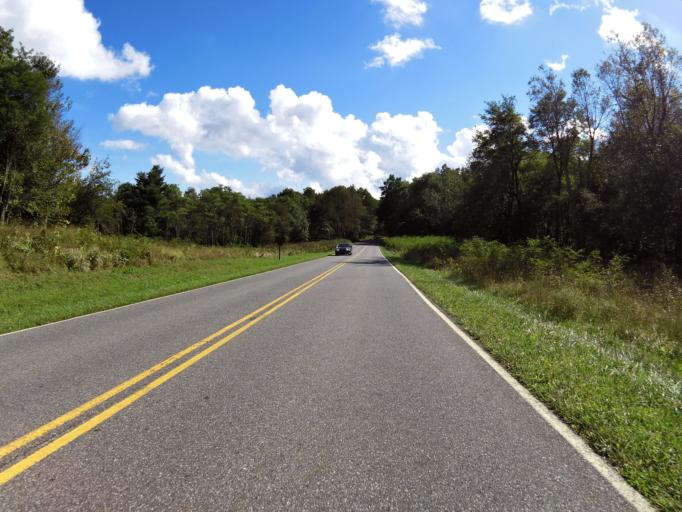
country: US
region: Virginia
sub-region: Page County
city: Stanley
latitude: 38.5459
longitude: -78.4149
